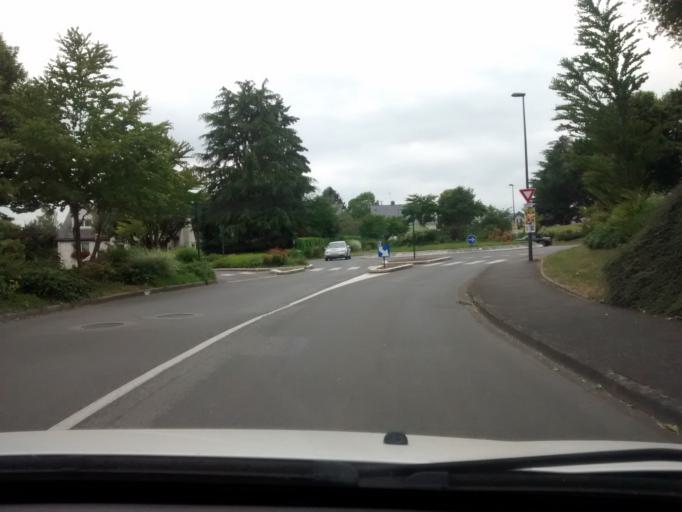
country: FR
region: Brittany
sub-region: Departement d'Ille-et-Vilaine
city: Cesson-Sevigne
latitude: 48.1207
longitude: -1.6026
